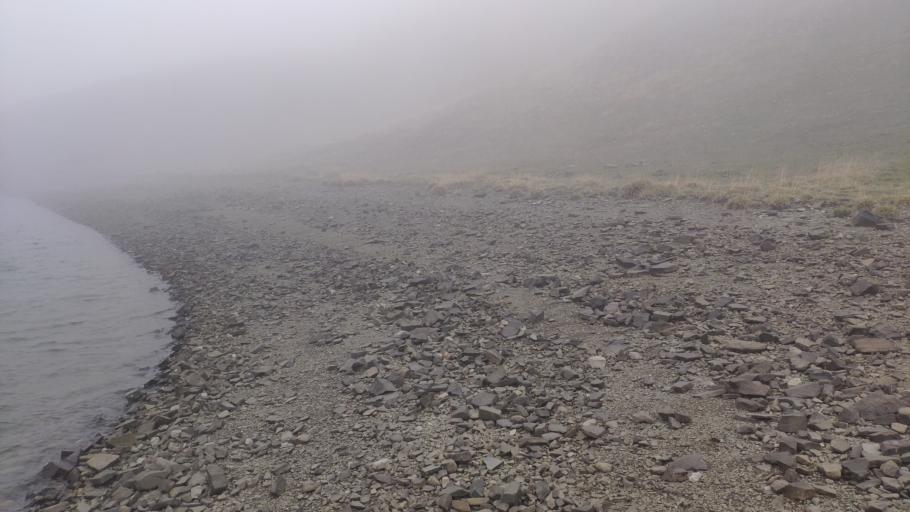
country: AL
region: Korce
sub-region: Rrethi i Kolonjes
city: Erseke
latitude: 40.3642
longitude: 20.7909
